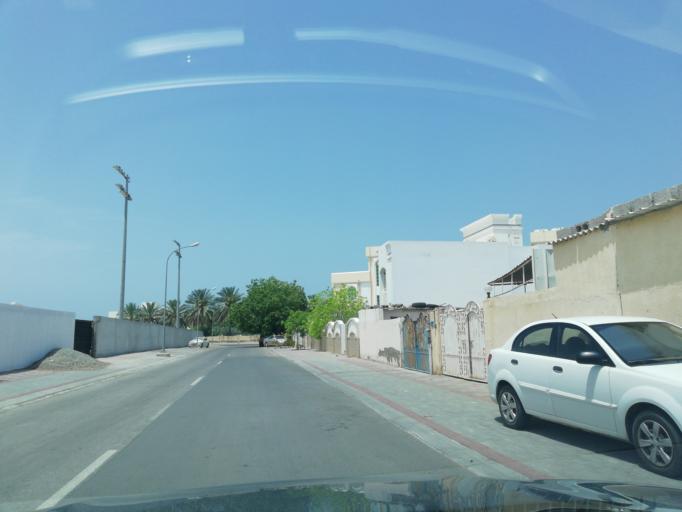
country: OM
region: Muhafazat Masqat
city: As Sib al Jadidah
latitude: 23.6613
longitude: 58.1950
